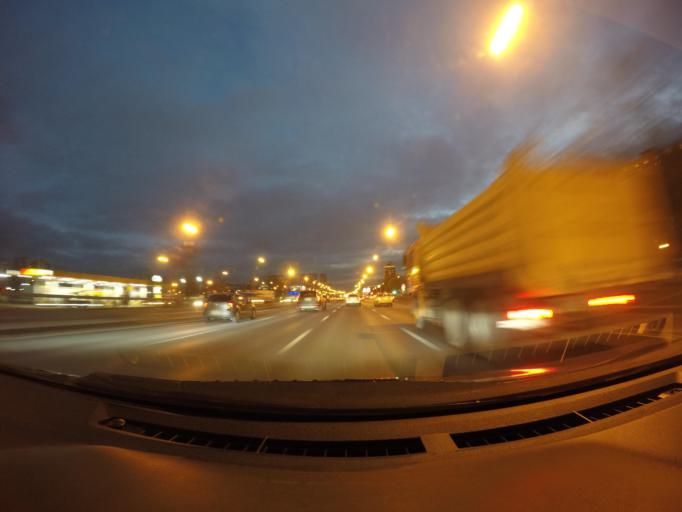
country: RU
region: Moscow
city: Orekhovo-Borisovo
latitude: 55.6128
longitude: 37.7164
